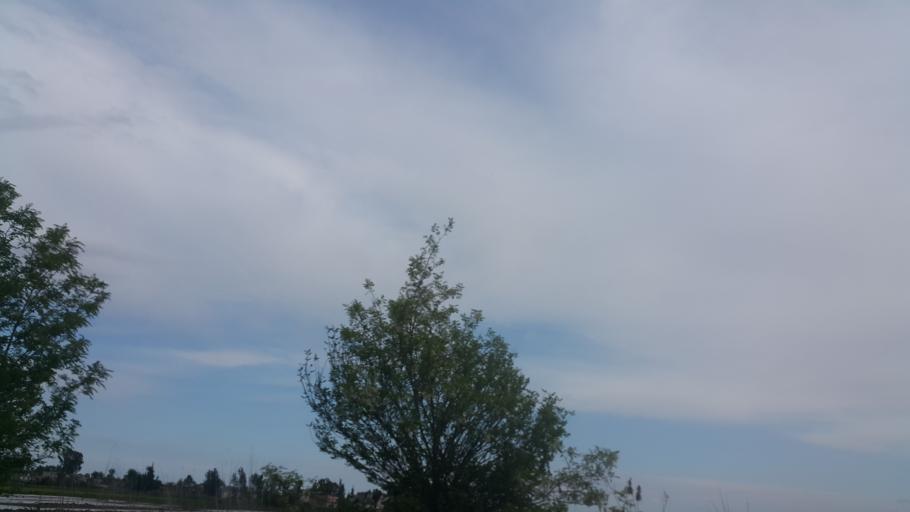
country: TR
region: Mersin
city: Yenice
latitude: 36.9632
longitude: 35.0209
